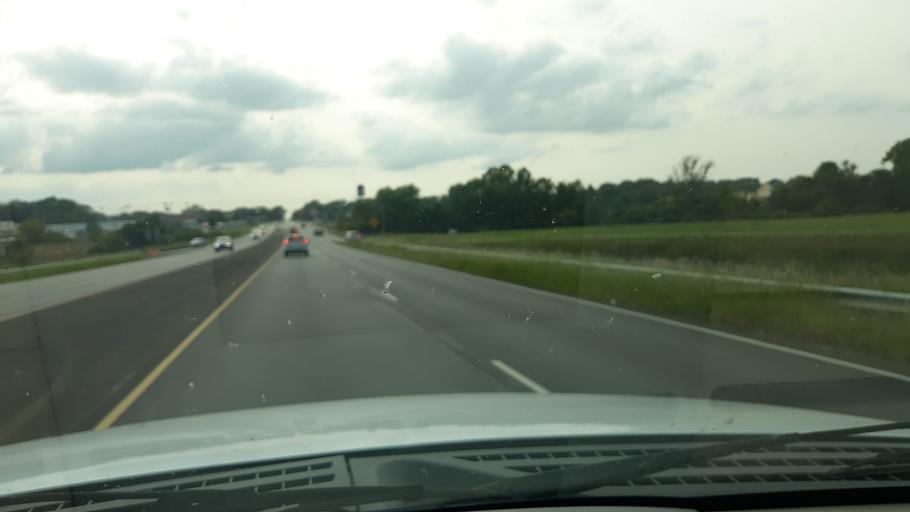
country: US
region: Indiana
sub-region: Gibson County
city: Princeton
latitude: 38.3556
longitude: -87.6005
